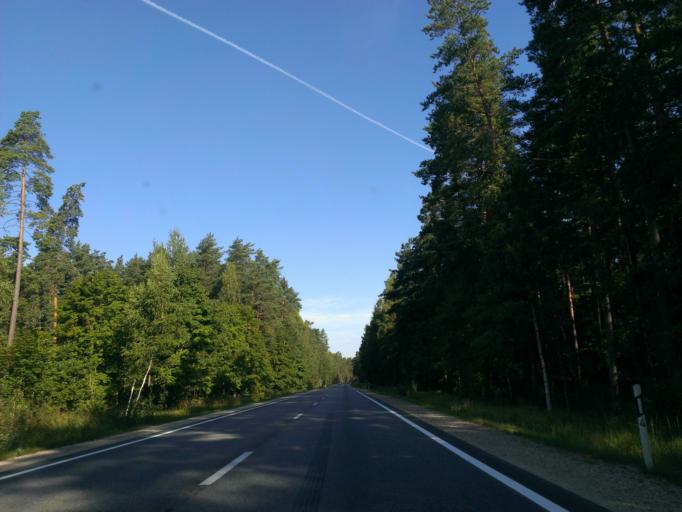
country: LV
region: Riga
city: Bergi
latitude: 56.9895
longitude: 24.3163
